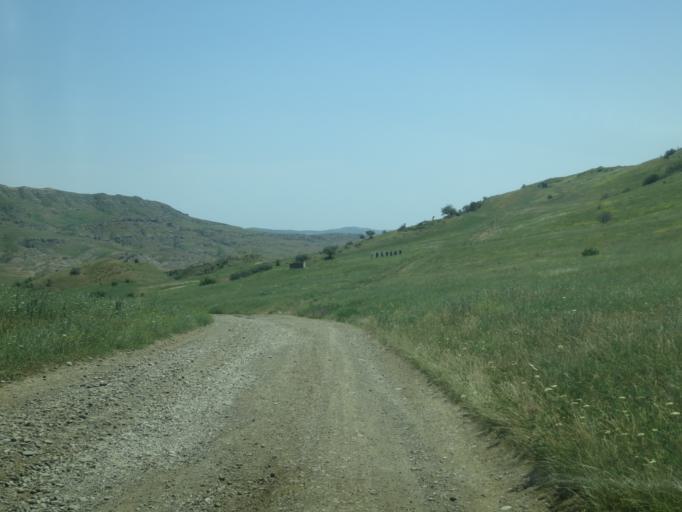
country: AZ
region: Agstafa
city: Saloglu
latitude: 41.4599
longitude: 45.3503
